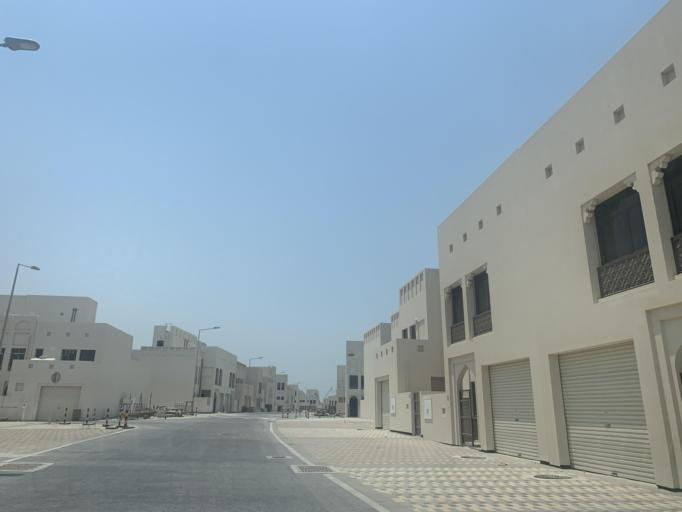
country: BH
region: Muharraq
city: Al Hadd
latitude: 26.2388
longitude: 50.6703
